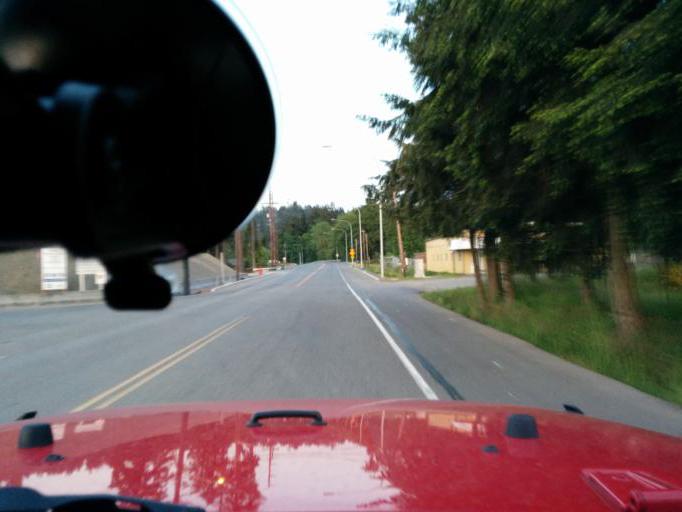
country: US
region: Washington
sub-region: King County
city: Sammamish
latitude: 47.6756
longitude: -122.0850
